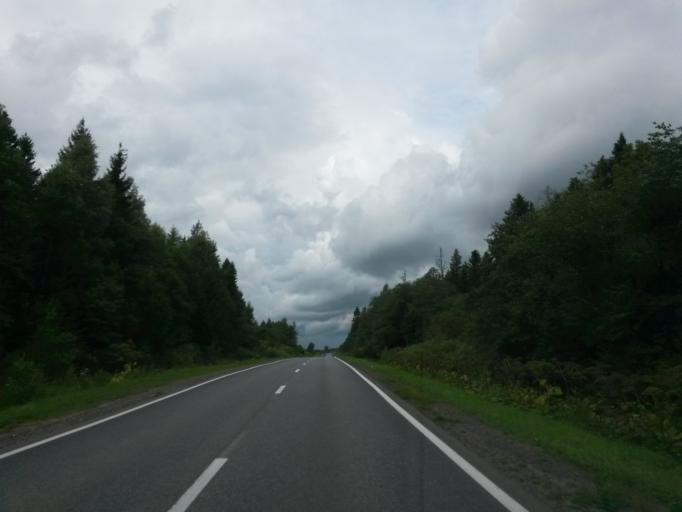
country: RU
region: Jaroslavl
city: Konstantinovskiy
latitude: 57.8257
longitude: 39.6779
